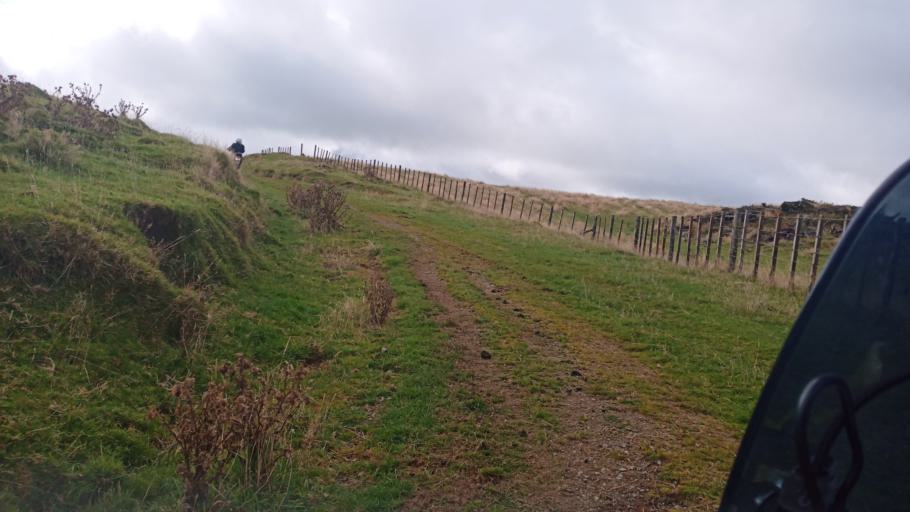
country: NZ
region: Gisborne
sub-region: Gisborne District
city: Gisborne
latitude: -38.4754
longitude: 177.5357
